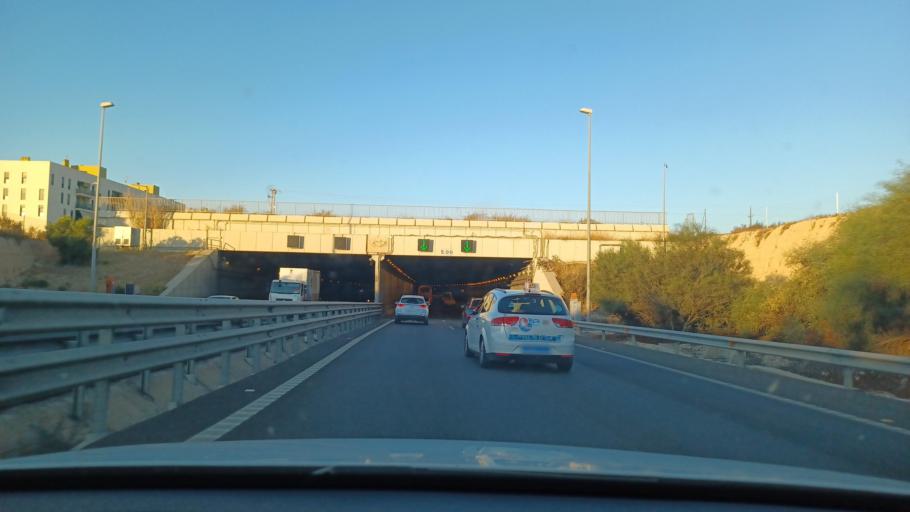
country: ES
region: Valencia
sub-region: Provincia de Alicante
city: San Juan de Alicante
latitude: 38.4143
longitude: -0.4314
